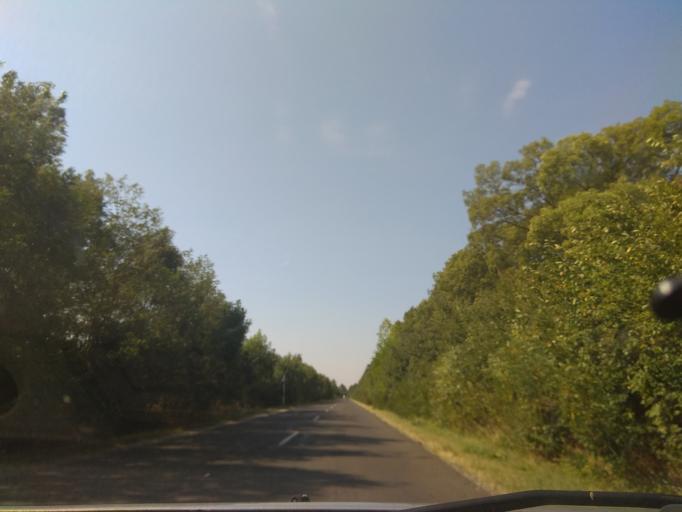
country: HU
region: Borsod-Abauj-Zemplen
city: Harsany
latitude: 47.9276
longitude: 20.7264
